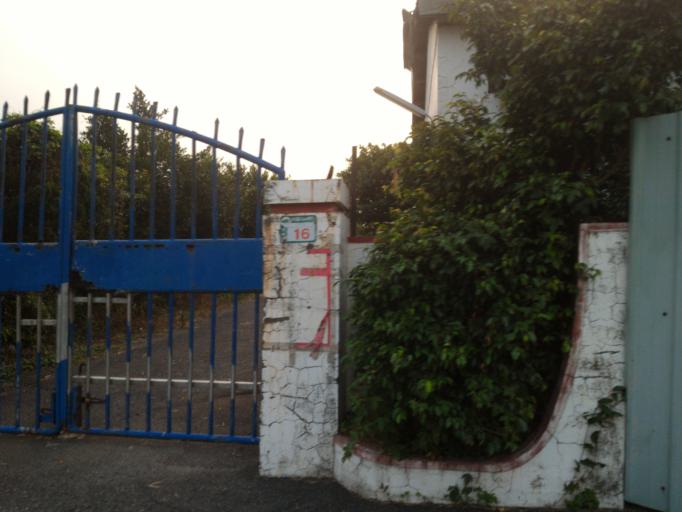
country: TW
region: Taiwan
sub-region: Taoyuan
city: Taoyuan
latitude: 24.9551
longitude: 121.3929
